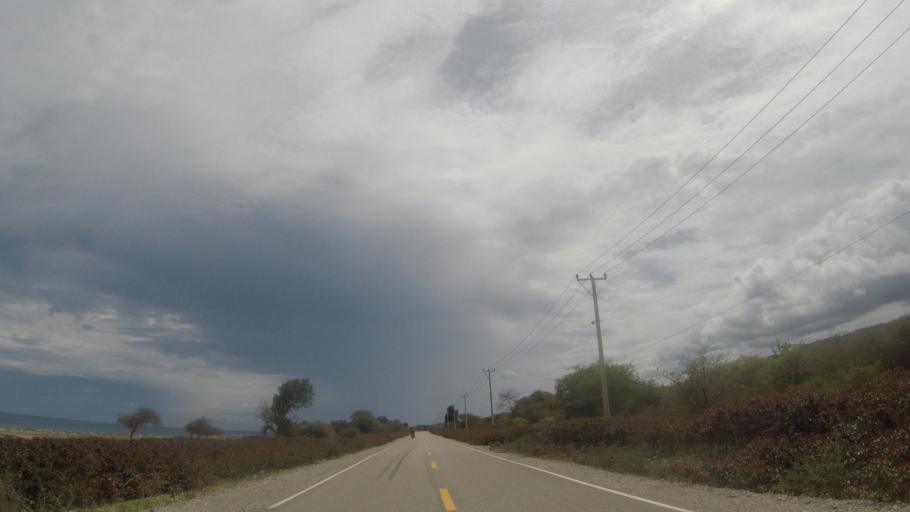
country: TL
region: Baucau
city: Baucau
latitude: -8.4584
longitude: 126.6147
